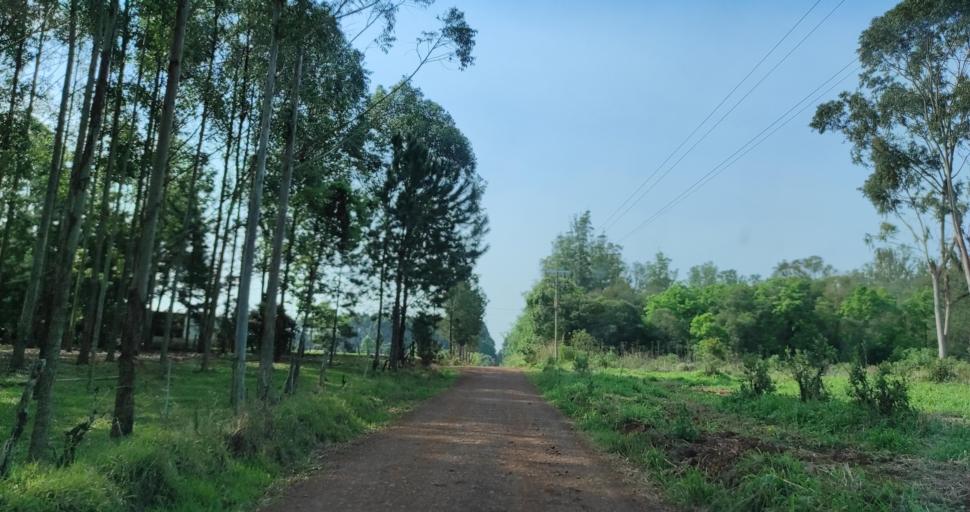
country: AR
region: Misiones
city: Capiovi
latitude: -26.8846
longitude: -55.0484
